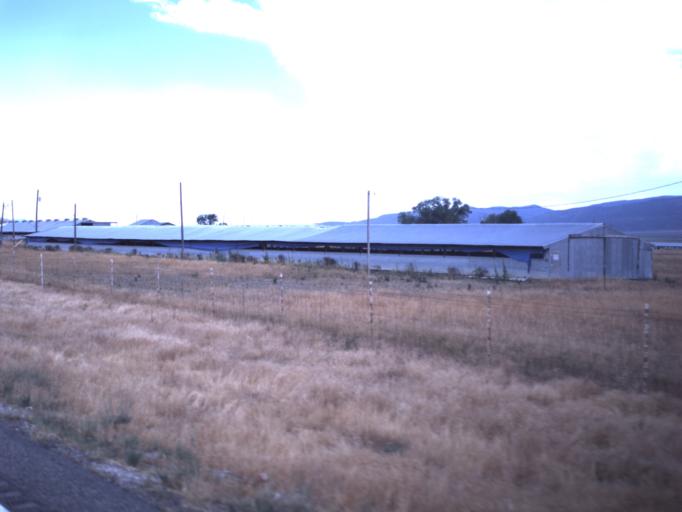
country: US
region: Utah
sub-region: Sanpete County
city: Ephraim
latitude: 39.4280
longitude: -111.5623
